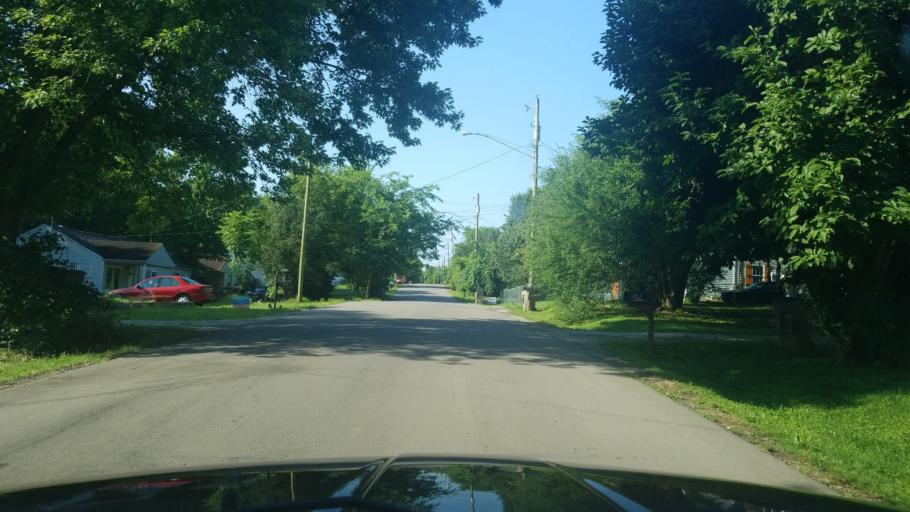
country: US
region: Tennessee
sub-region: Davidson County
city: Oak Hill
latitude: 36.1059
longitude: -86.7491
